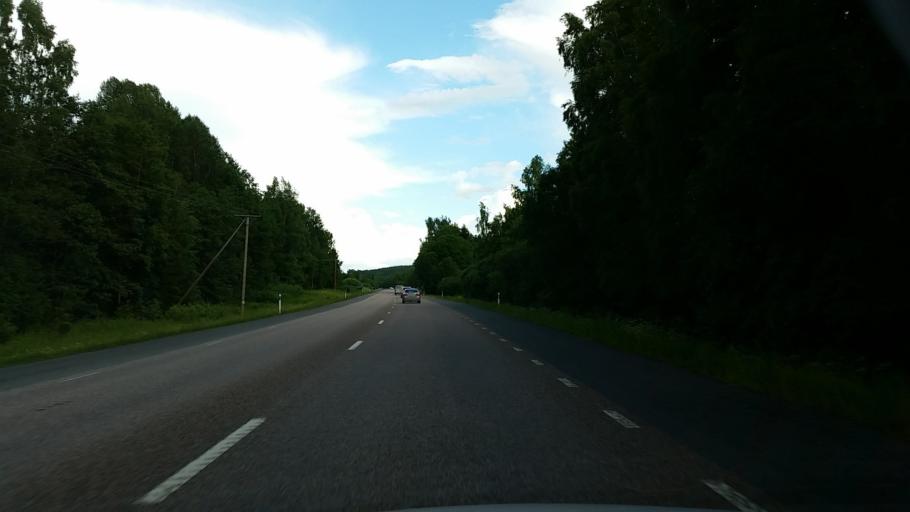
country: SE
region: Vaestmanland
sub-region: Fagersta Kommun
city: Fagersta
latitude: 59.9884
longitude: 15.6755
